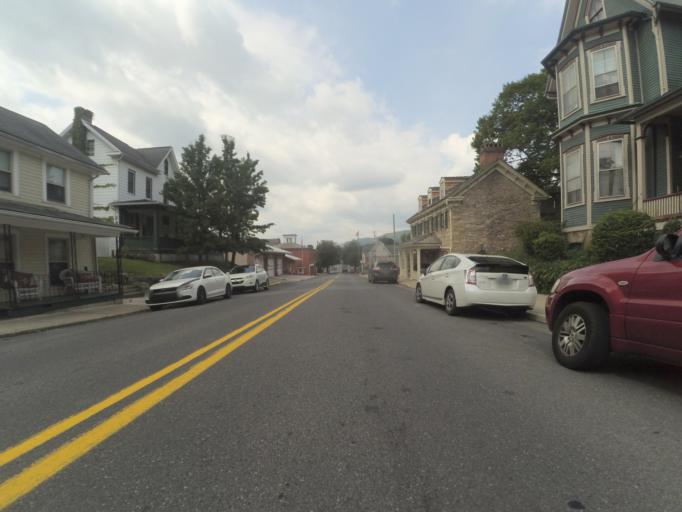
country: US
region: Pennsylvania
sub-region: Centre County
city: Bellefonte
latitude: 40.9138
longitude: -77.7765
